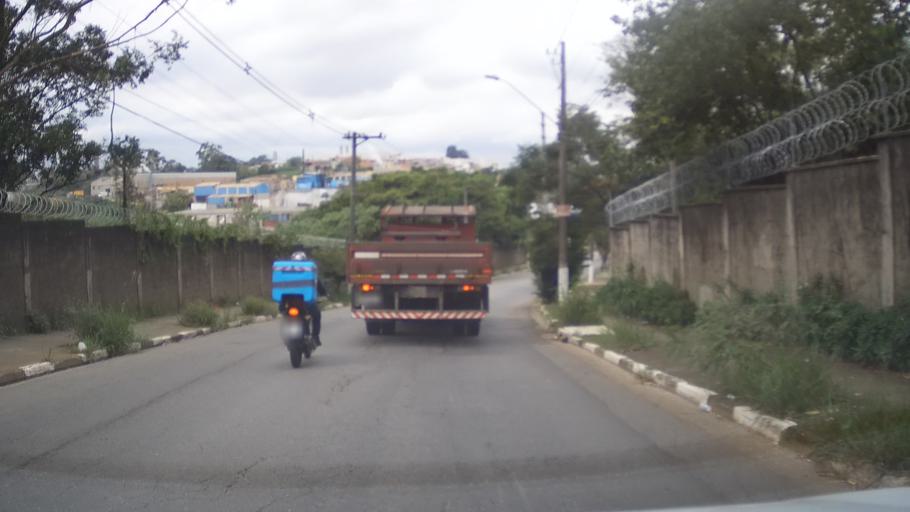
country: BR
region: Sao Paulo
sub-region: Itaquaquecetuba
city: Itaquaquecetuba
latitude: -23.4435
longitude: -46.3952
